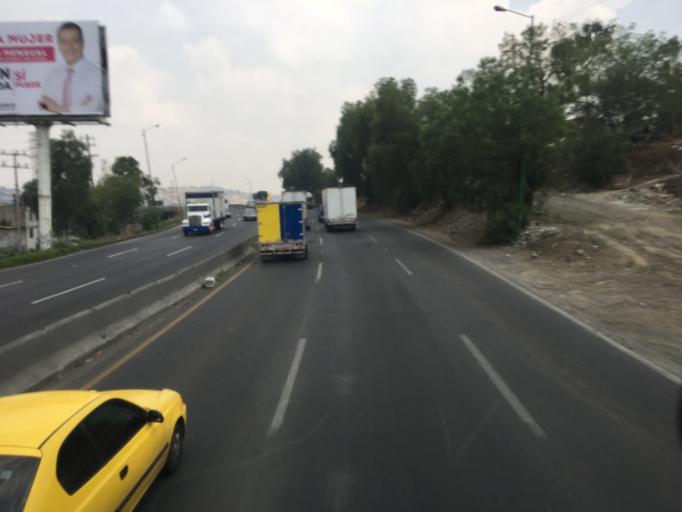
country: MX
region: Mexico
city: Tlalnepantla
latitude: 19.5597
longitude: -99.1925
